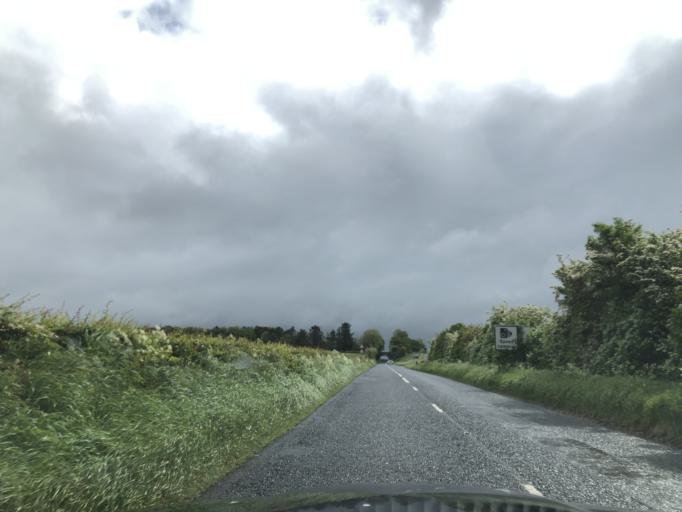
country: GB
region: Northern Ireland
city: Bushmills
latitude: 55.1606
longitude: -6.3815
